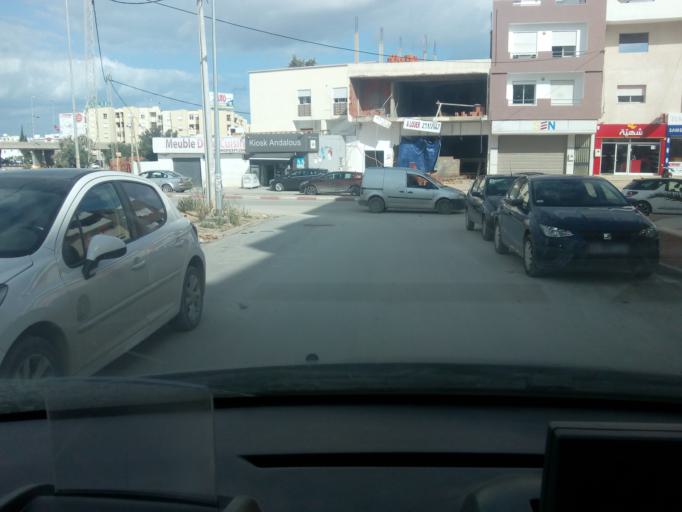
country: TN
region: Ariana
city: Ariana
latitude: 36.8776
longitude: 10.1783
